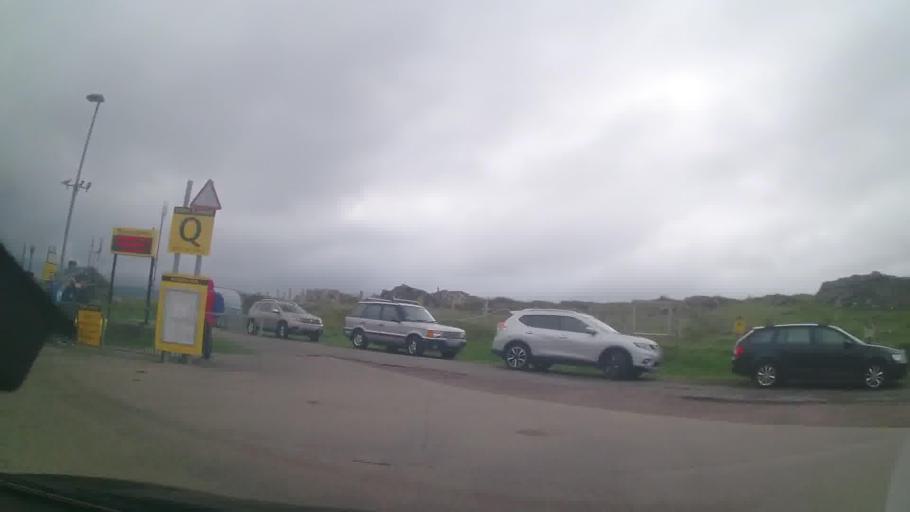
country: GB
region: Scotland
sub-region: Argyll and Bute
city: Isle Of Mull
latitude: 56.6888
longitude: -6.0951
